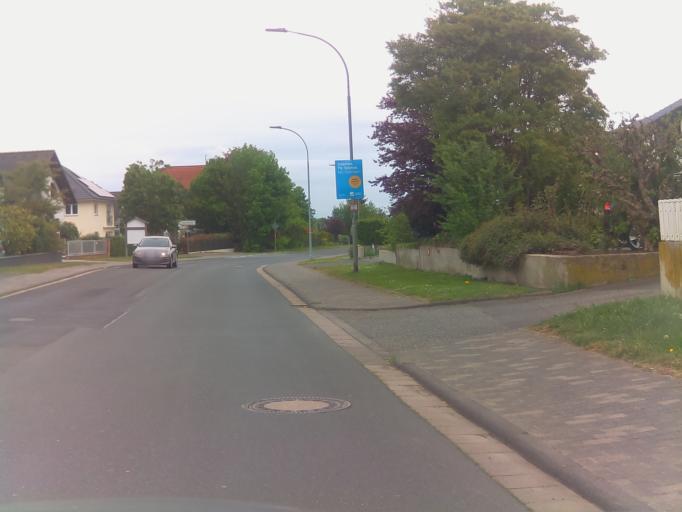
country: DE
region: Hesse
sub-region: Regierungsbezirk Darmstadt
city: Butzbach
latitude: 50.4132
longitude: 8.6826
